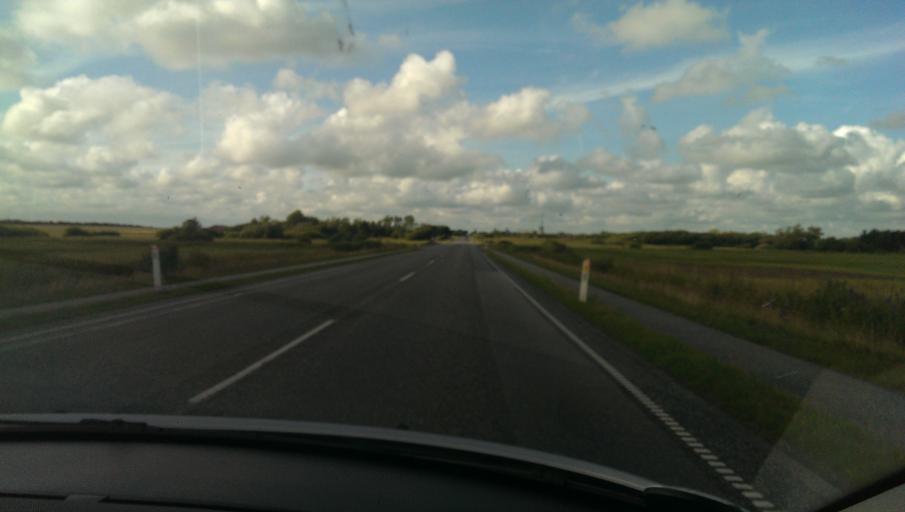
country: DK
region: Central Jutland
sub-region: Ringkobing-Skjern Kommune
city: Ringkobing
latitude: 56.1329
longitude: 8.2809
